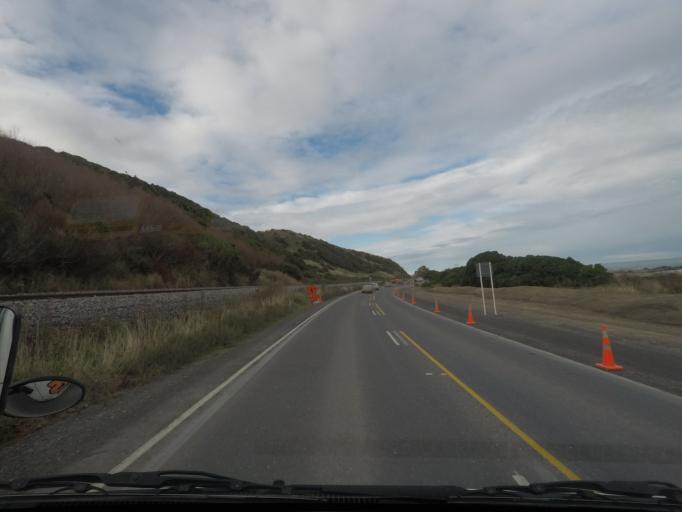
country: NZ
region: Canterbury
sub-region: Kaikoura District
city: Kaikoura
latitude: -42.2163
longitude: 173.8628
